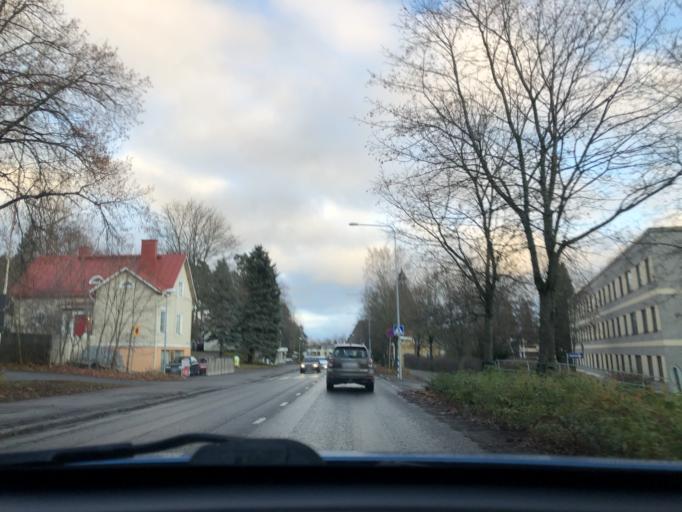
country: FI
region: Pirkanmaa
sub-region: Tampere
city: Kangasala
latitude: 61.4637
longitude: 24.0655
